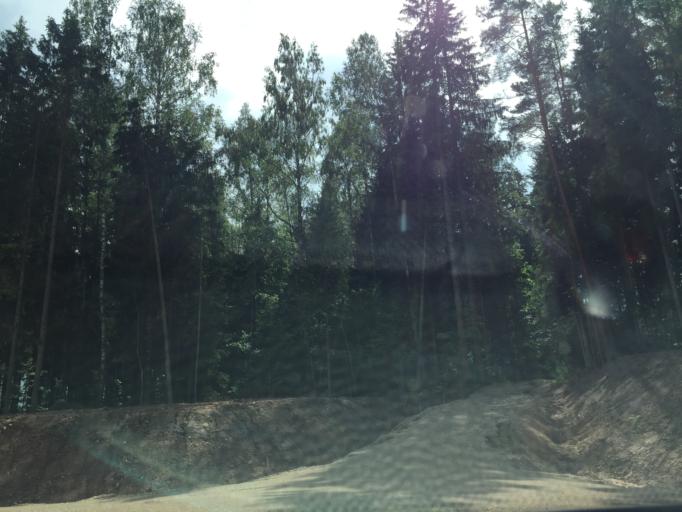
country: LV
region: Tukuma Rajons
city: Tukums
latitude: 57.0250
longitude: 23.2488
